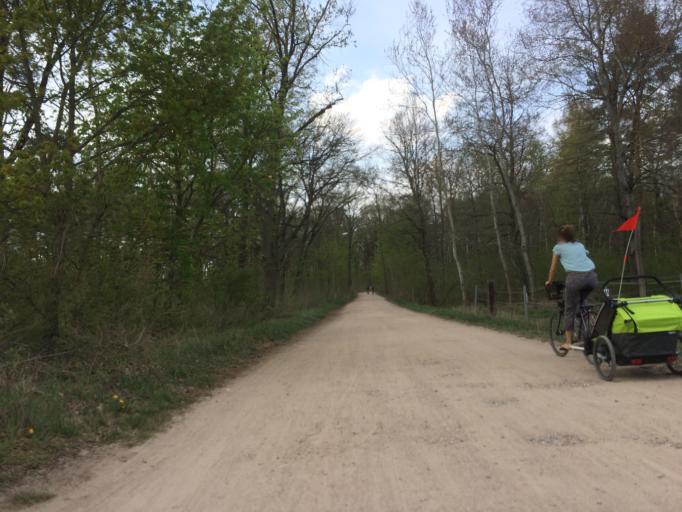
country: DE
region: Berlin
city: Buch
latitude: 52.6807
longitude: 13.4763
